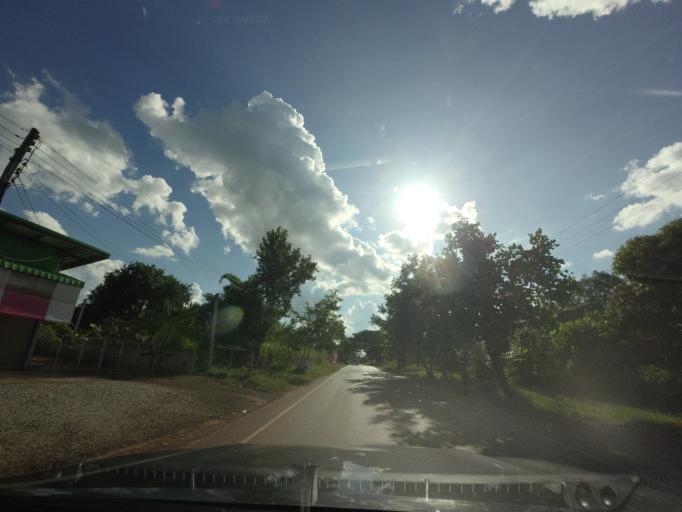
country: TH
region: Changwat Udon Thani
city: Ban Dung
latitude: 17.7443
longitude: 103.3157
